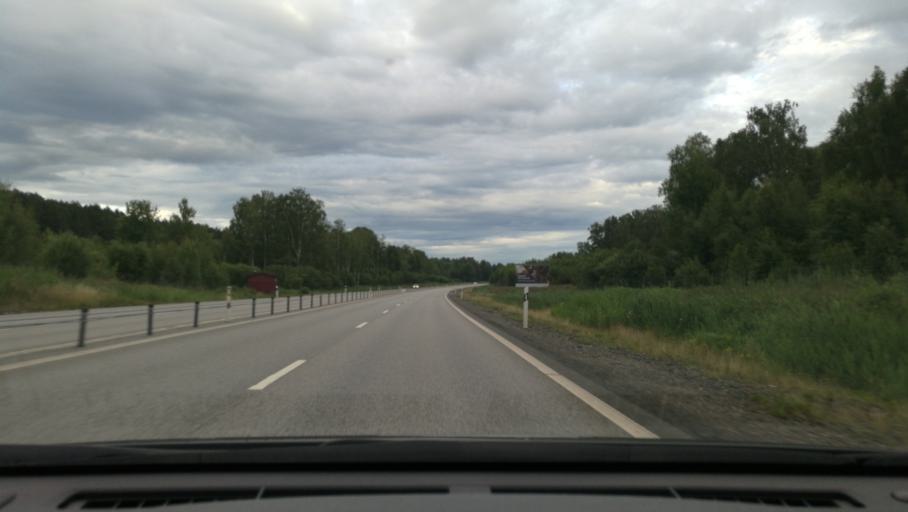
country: SE
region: OEstergoetland
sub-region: Norrkopings Kommun
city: Svartinge
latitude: 58.6455
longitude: 16.0716
